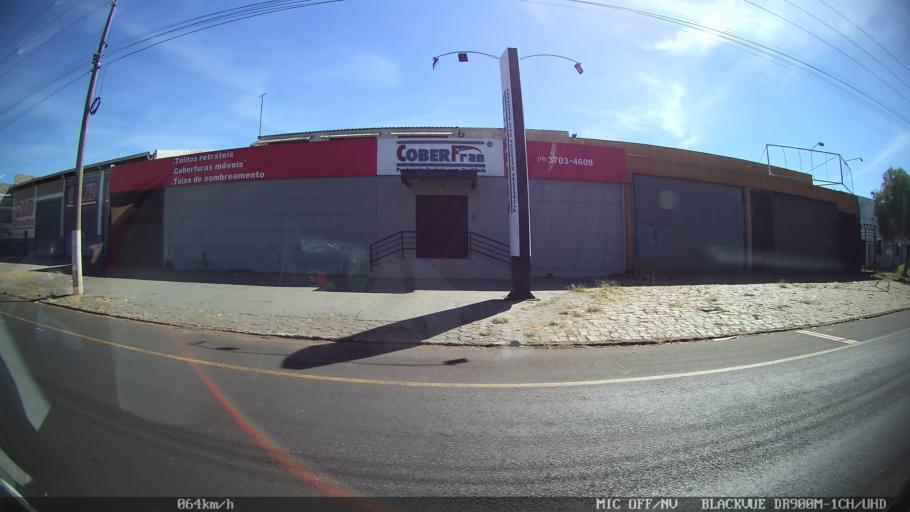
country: BR
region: Sao Paulo
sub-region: Franca
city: Franca
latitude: -20.5550
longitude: -47.4387
